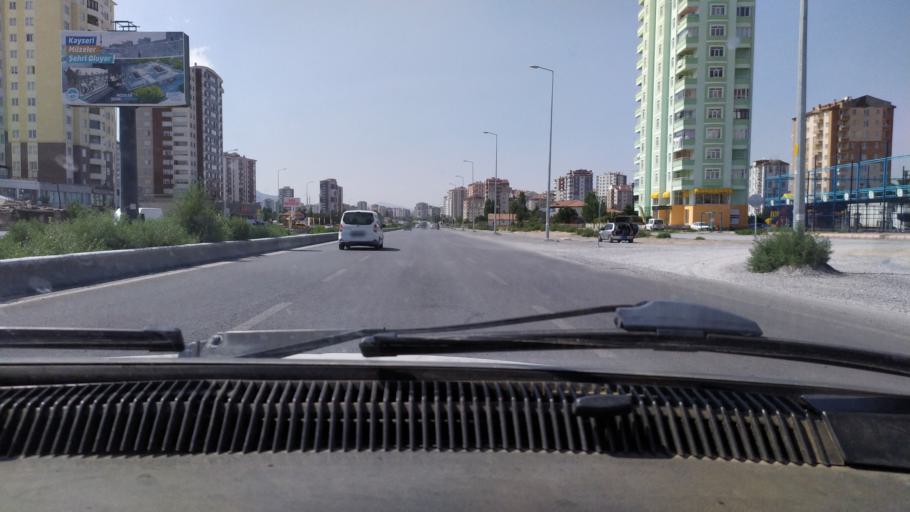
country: TR
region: Kayseri
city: Talas
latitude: 38.7207
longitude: 35.5424
